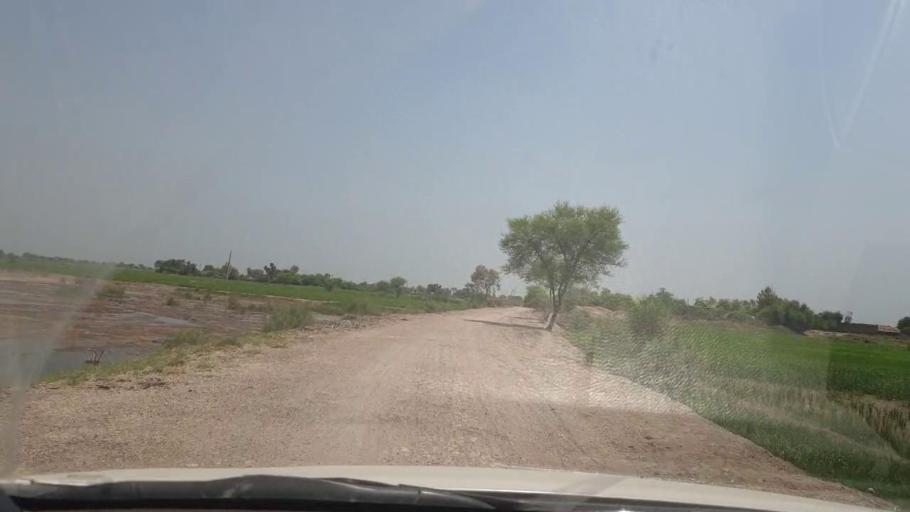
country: PK
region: Sindh
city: Lakhi
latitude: 27.8814
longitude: 68.7449
